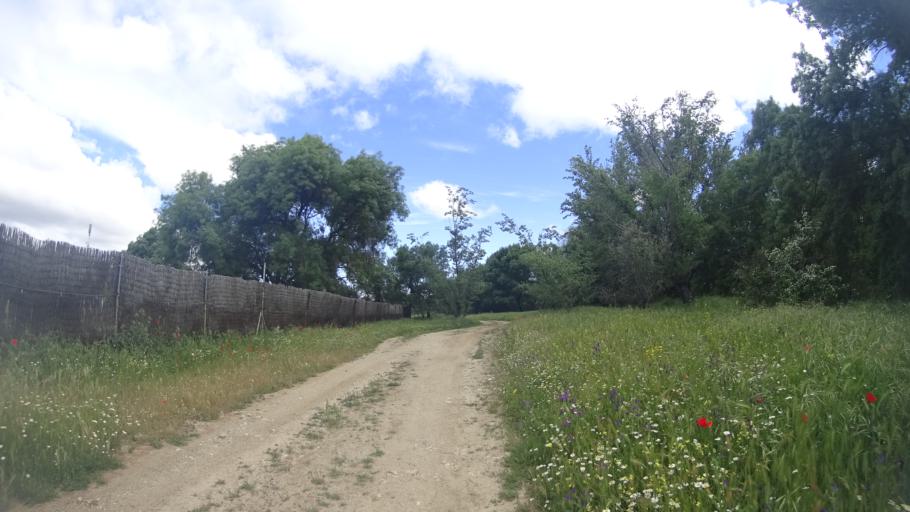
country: ES
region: Madrid
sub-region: Provincia de Madrid
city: Brunete
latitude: 40.4064
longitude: -3.9472
